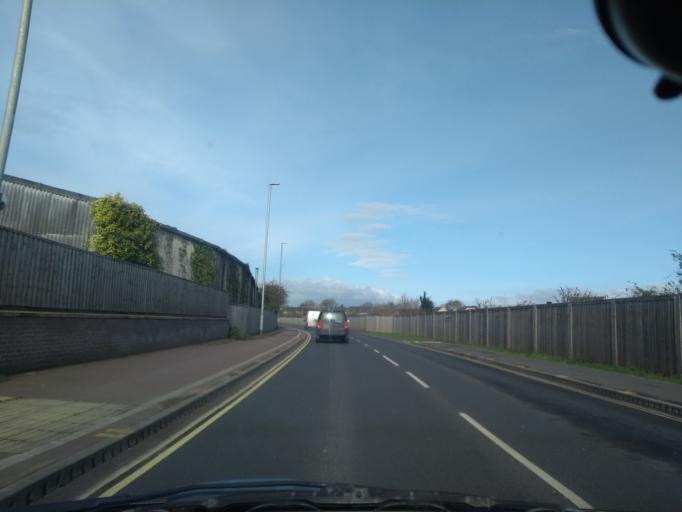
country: GB
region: England
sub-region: Somerset
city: Taunton
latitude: 51.0224
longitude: -3.1048
